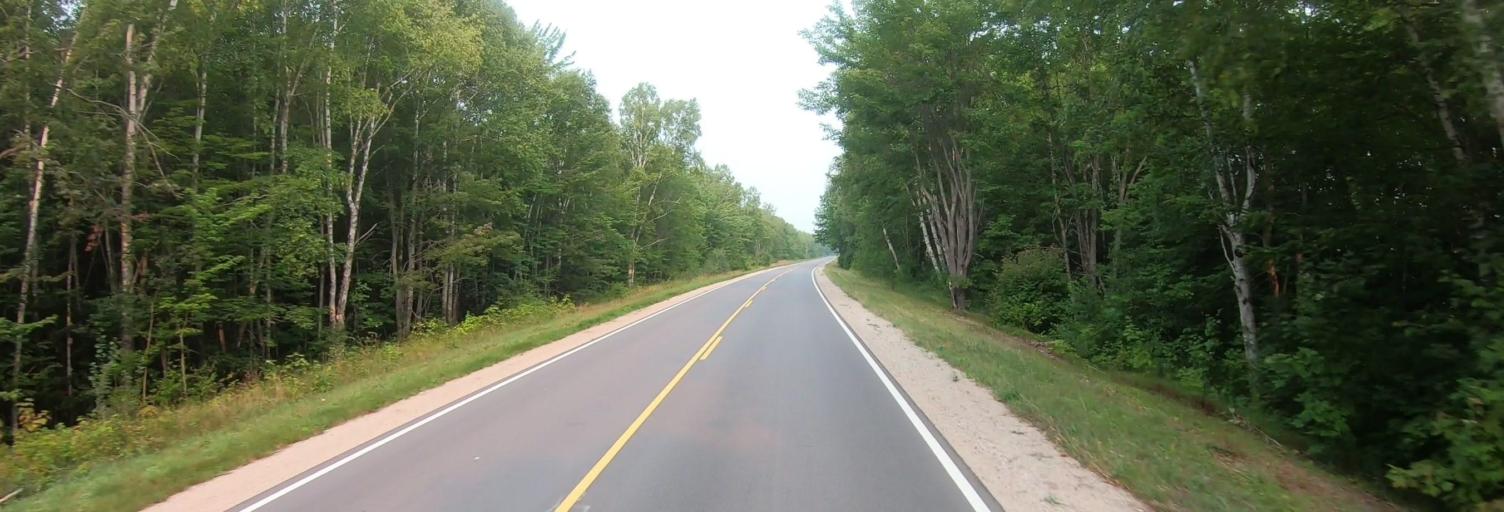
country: US
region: Michigan
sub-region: Luce County
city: Newberry
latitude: 46.4792
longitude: -85.0150
